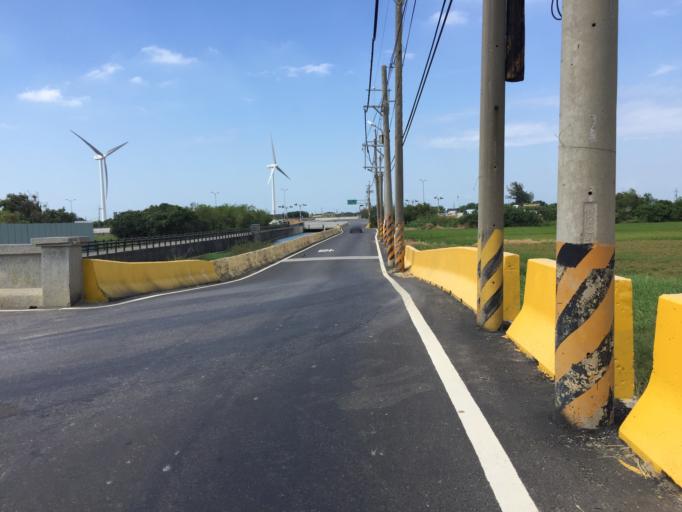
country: TW
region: Taiwan
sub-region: Hsinchu
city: Hsinchu
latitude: 24.7627
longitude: 120.9106
